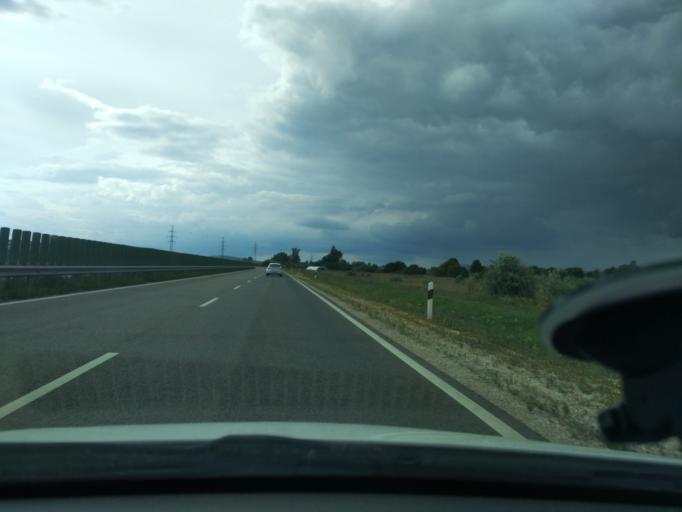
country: HU
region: Fejer
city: Sarszentmihaly
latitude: 47.2023
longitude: 18.3422
